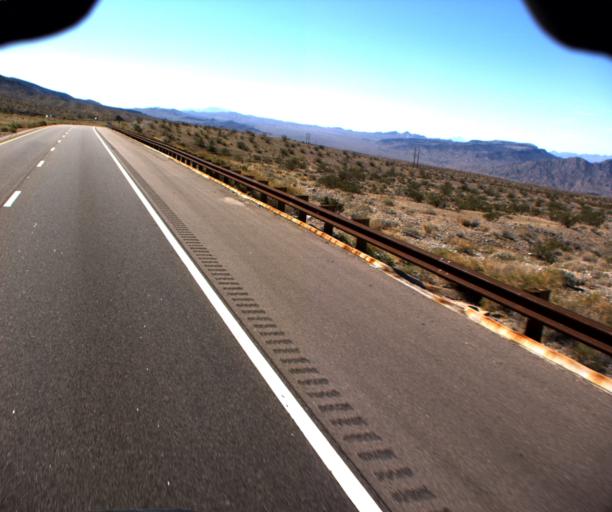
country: US
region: Nevada
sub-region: Clark County
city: Boulder City
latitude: 35.9344
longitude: -114.6376
